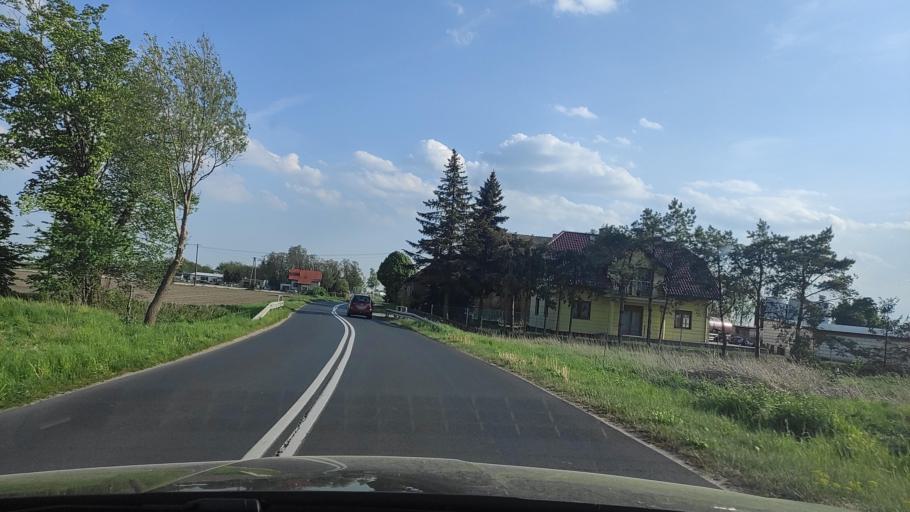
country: PL
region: Greater Poland Voivodeship
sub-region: Powiat poznanski
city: Kleszczewo
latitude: 52.3498
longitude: 17.1711
